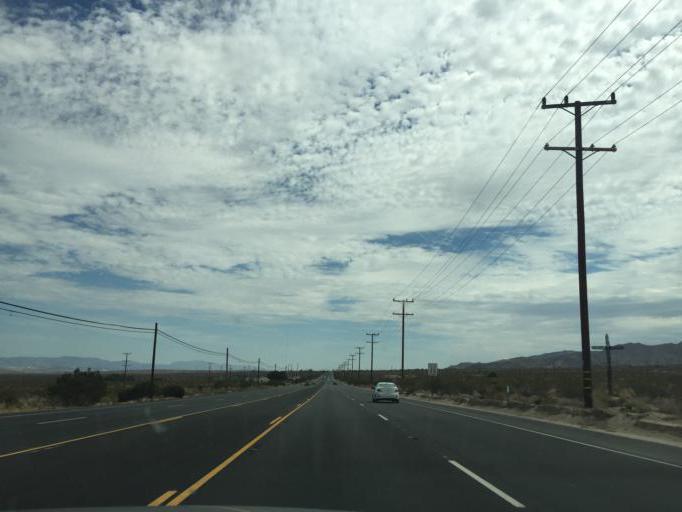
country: US
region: California
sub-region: San Bernardino County
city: Joshua Tree
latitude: 34.1351
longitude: -116.1926
